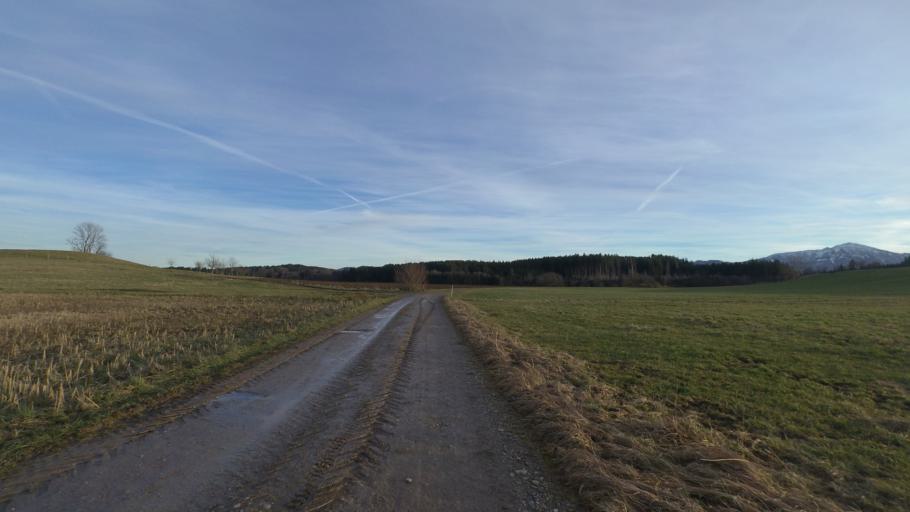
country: DE
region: Bavaria
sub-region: Upper Bavaria
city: Chieming
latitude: 47.8847
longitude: 12.5426
